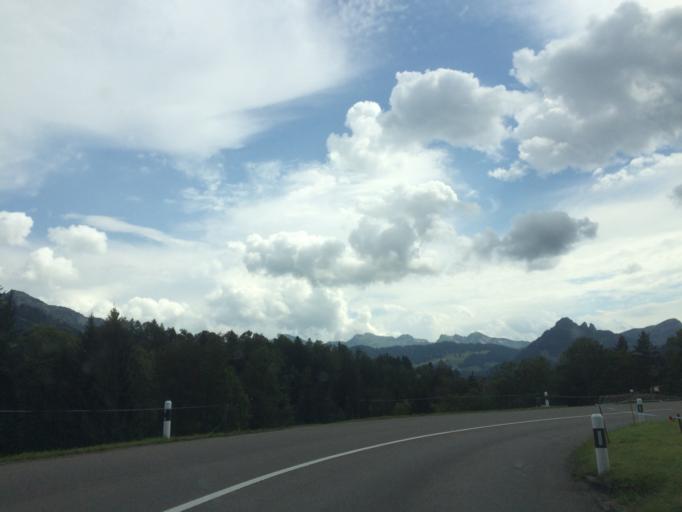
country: CH
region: Saint Gallen
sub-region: Wahlkreis Toggenburg
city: Krummenau
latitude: 47.2377
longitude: 9.2086
